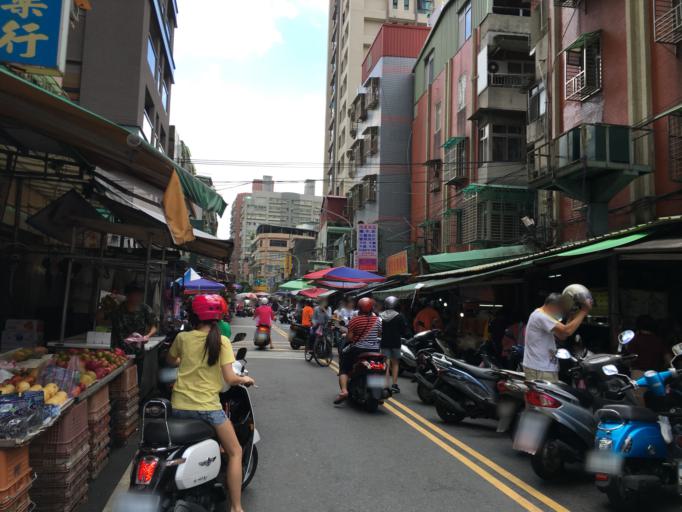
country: TW
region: Taipei
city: Taipei
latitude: 25.0806
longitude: 121.4906
